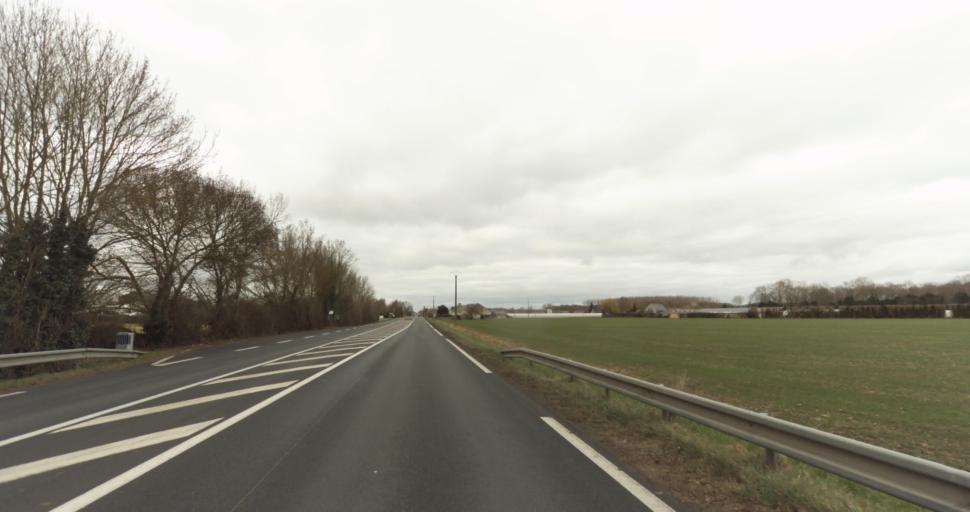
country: FR
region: Pays de la Loire
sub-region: Departement de Maine-et-Loire
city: Vivy
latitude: 47.3137
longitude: -0.0443
